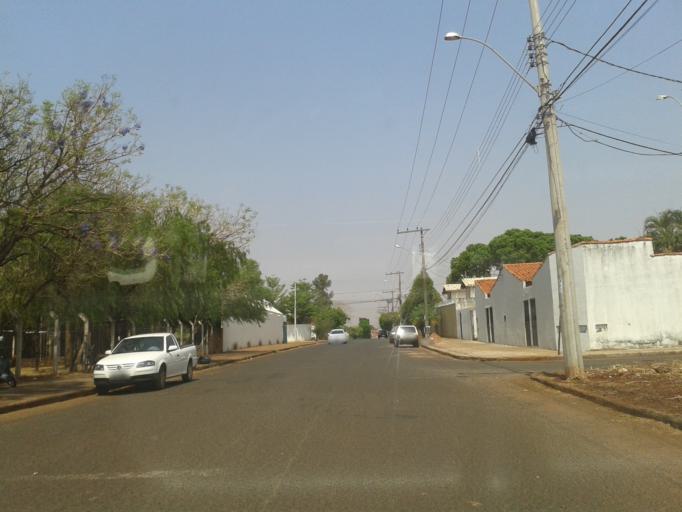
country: BR
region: Minas Gerais
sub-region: Ituiutaba
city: Ituiutaba
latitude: -18.9684
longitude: -49.4459
